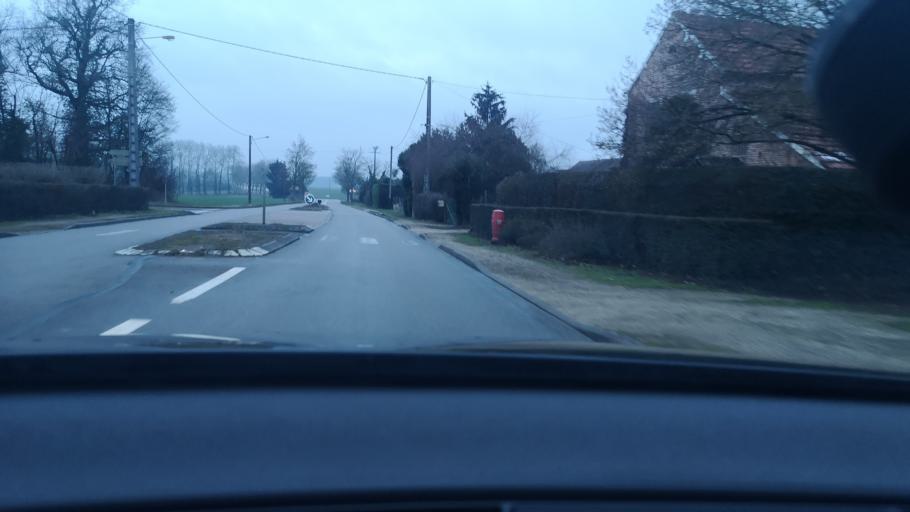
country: FR
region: Bourgogne
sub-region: Departement de la Cote-d'Or
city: Seurre
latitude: 47.0644
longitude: 5.0961
